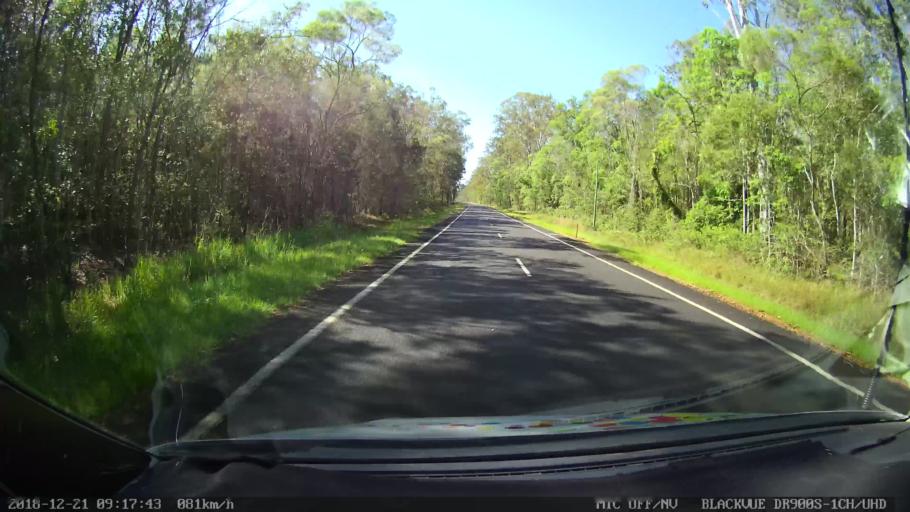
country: AU
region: New South Wales
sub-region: Clarence Valley
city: Maclean
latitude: -29.2956
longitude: 152.9917
